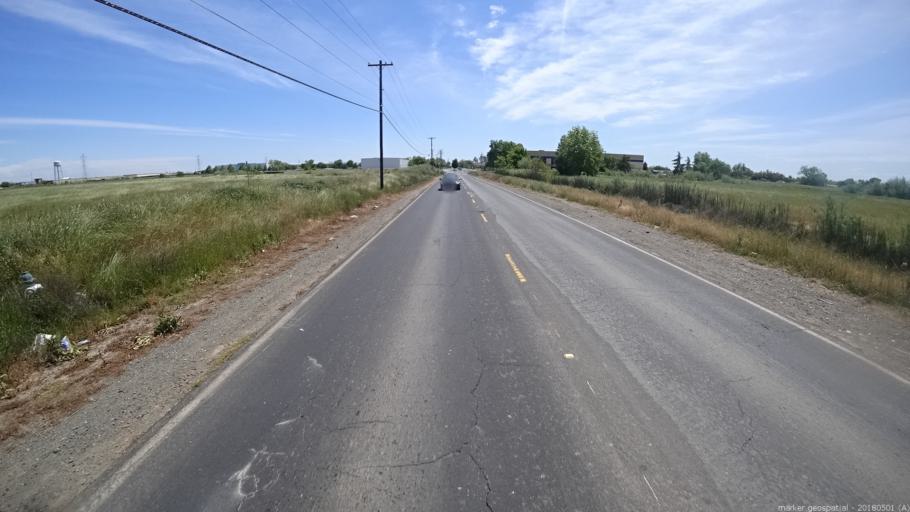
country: US
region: California
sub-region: Sacramento County
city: Rio Linda
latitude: 38.6624
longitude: -121.4292
